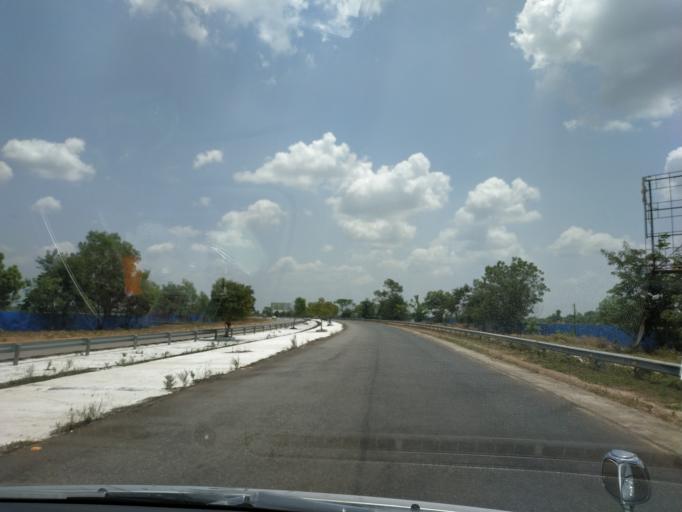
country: MM
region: Bago
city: Thanatpin
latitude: 17.1267
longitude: 96.1958
